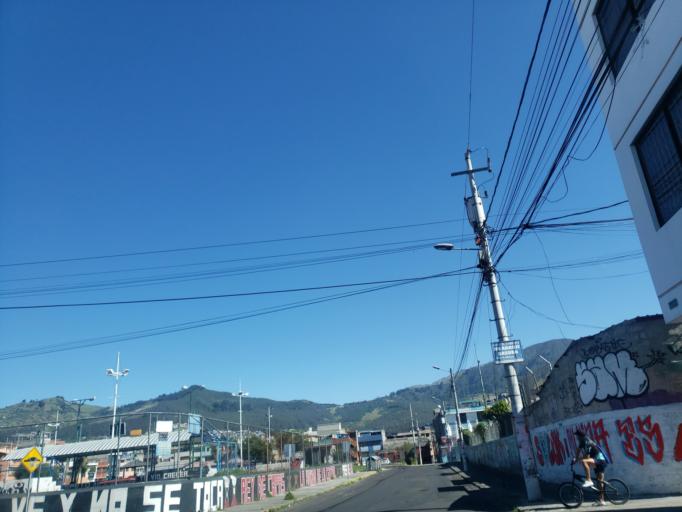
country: EC
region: Pichincha
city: Quito
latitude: -0.2719
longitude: -78.5396
